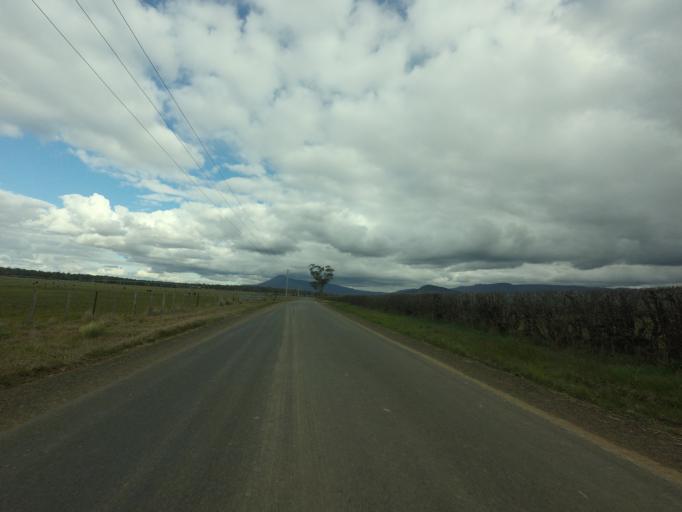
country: AU
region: Tasmania
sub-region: Northern Midlands
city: Longford
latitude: -41.7902
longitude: 147.1128
